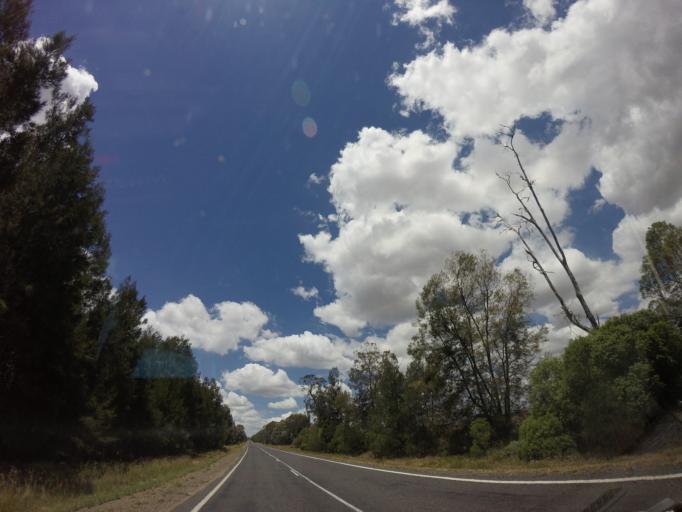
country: AU
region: Queensland
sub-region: Toowoomba
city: Oakey
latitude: -27.9503
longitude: 151.1418
